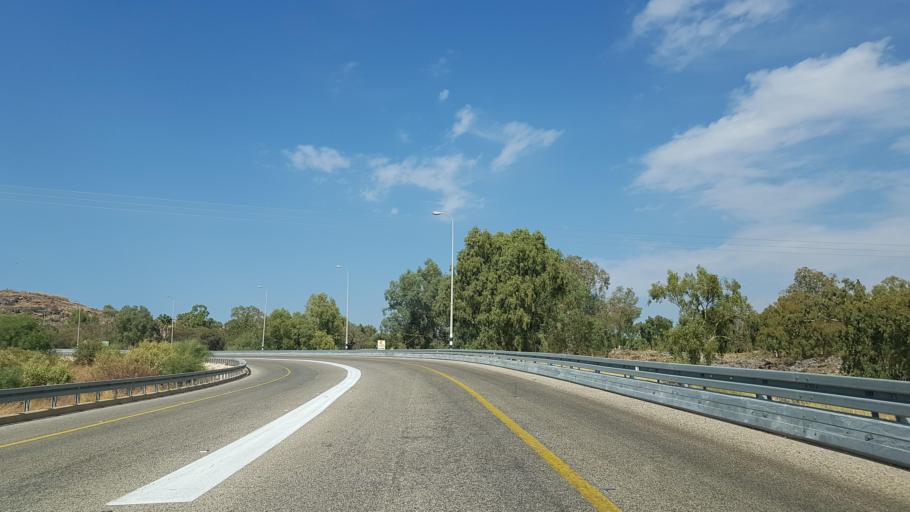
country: SY
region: Quneitra
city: Al Butayhah
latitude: 32.9105
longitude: 35.5980
